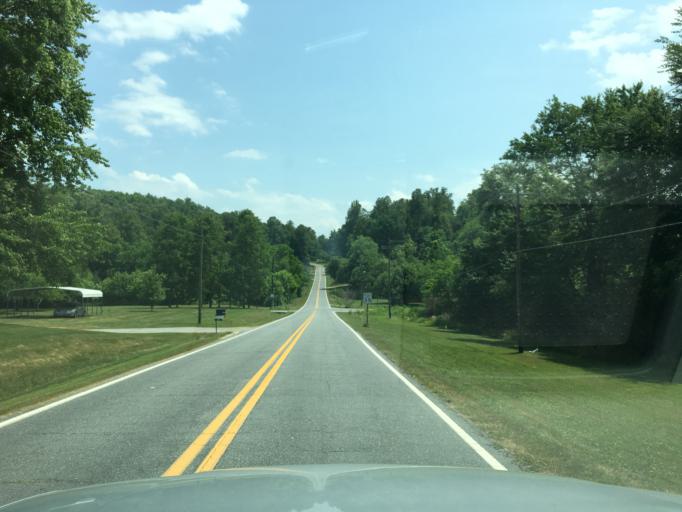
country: US
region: North Carolina
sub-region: McDowell County
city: West Marion
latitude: 35.6113
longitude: -81.9819
